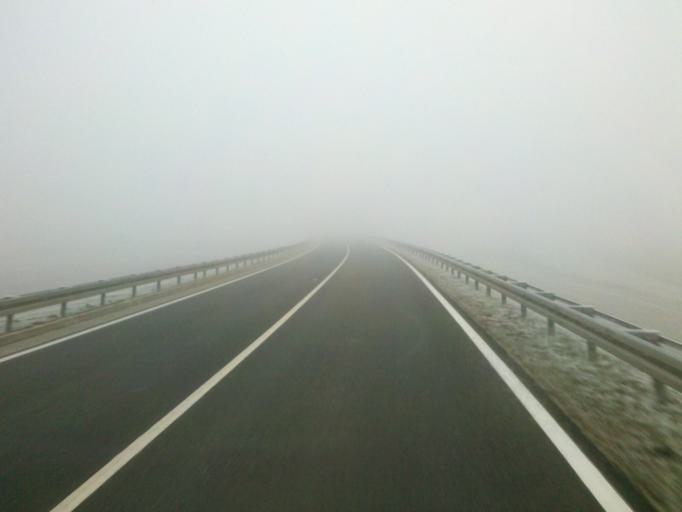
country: HR
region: Varazdinska
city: Jalkovec
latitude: 46.2873
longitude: 16.3113
